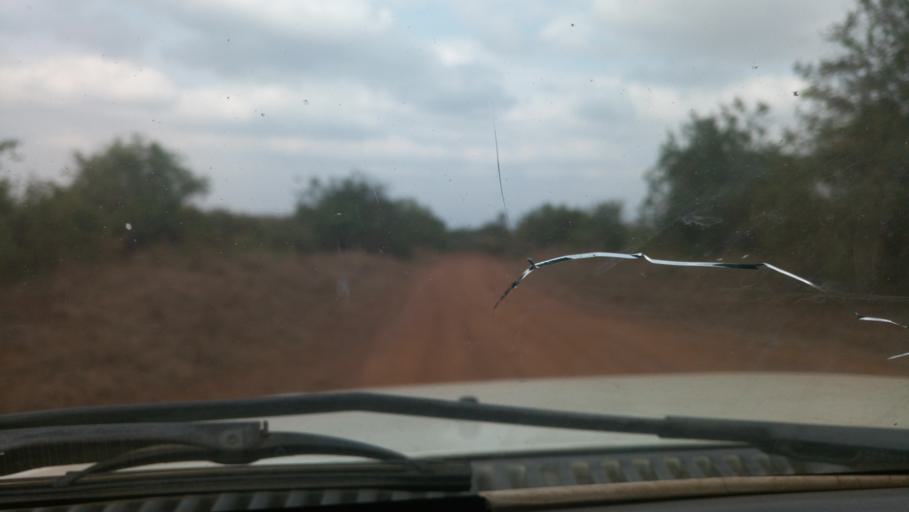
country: KE
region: Nairobi Area
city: Nairobi
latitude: -1.3572
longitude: 36.7931
